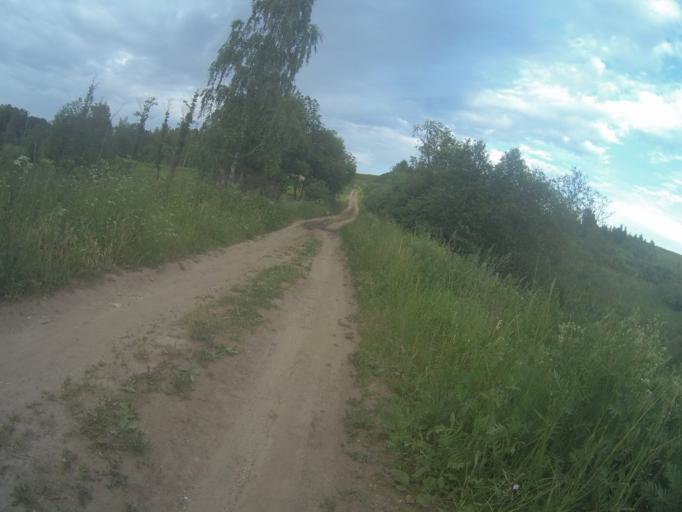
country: RU
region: Vladimir
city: Vladimir
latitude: 56.2126
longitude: 40.3938
